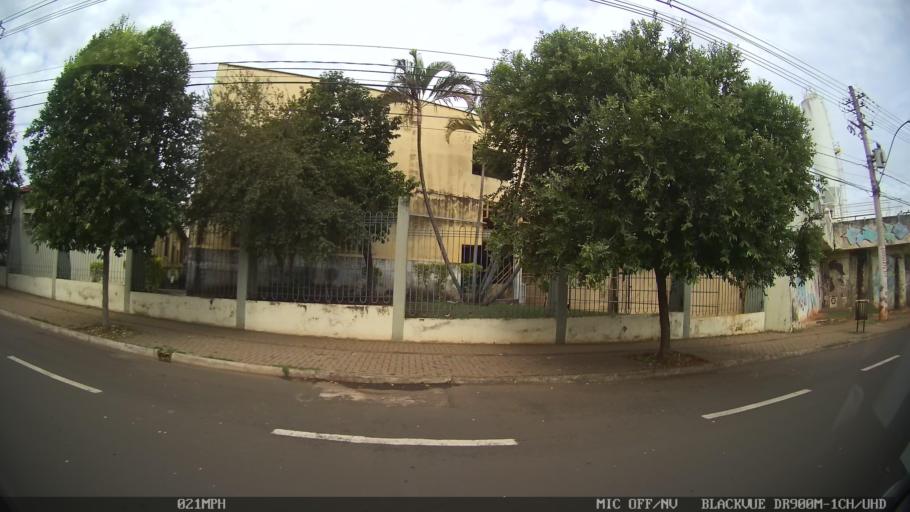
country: BR
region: Sao Paulo
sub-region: Piracicaba
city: Piracicaba
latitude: -22.7170
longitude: -47.6515
